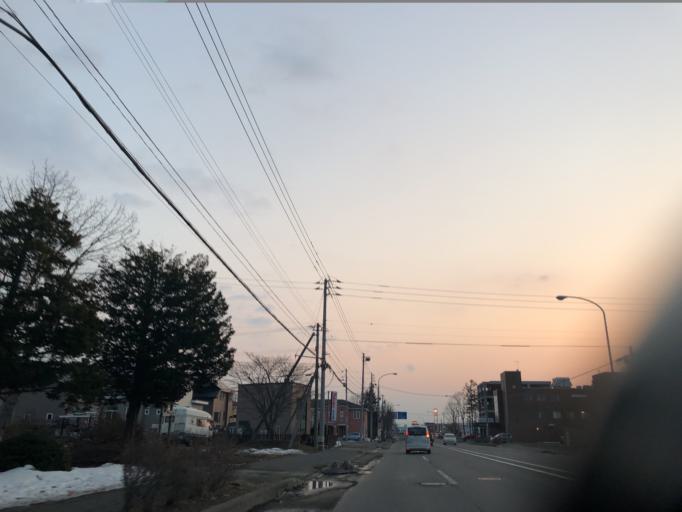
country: JP
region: Hokkaido
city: Chitose
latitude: 42.8270
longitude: 141.6729
